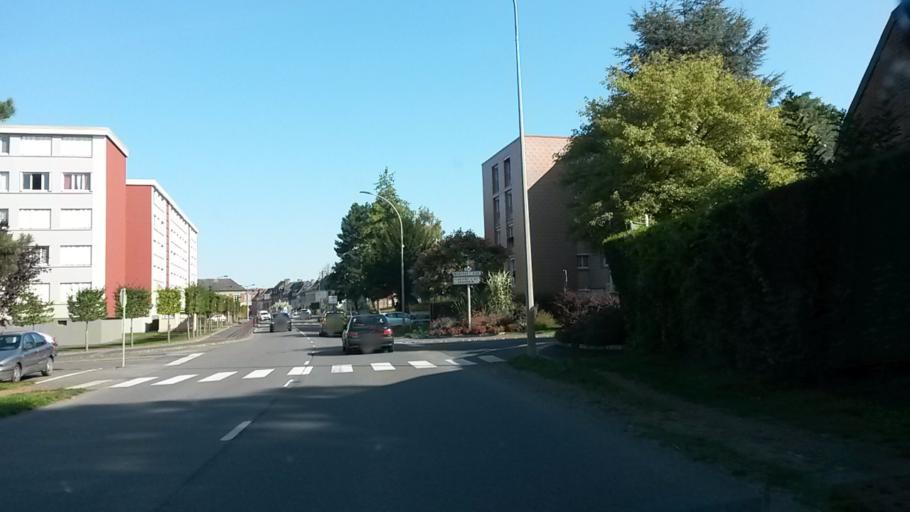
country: FR
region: Picardie
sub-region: Departement de l'Aisne
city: Guise
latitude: 49.8990
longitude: 3.6310
